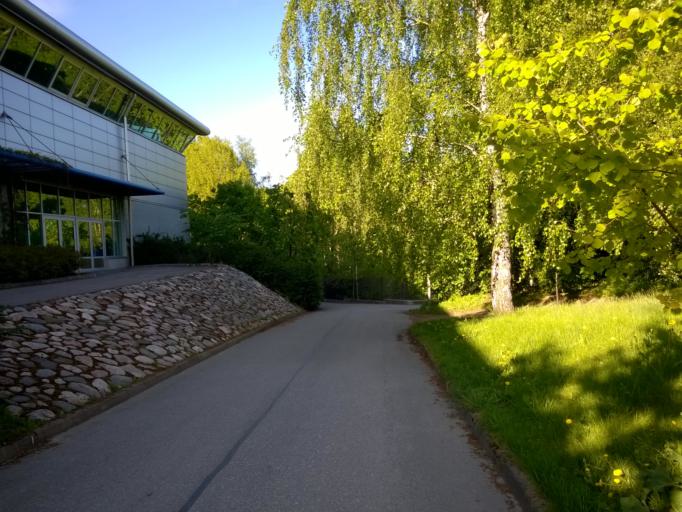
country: FI
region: Uusimaa
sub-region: Helsinki
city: Helsinki
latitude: 60.1995
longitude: 24.9483
